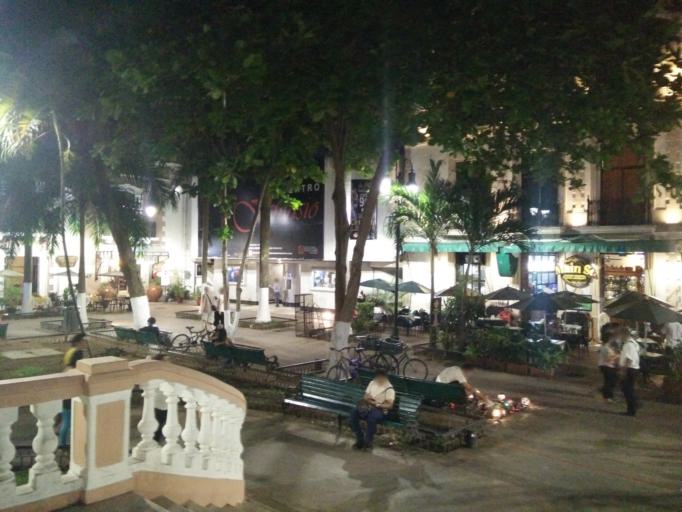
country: MX
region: Yucatan
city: Merida
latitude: 20.9684
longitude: -89.6226
